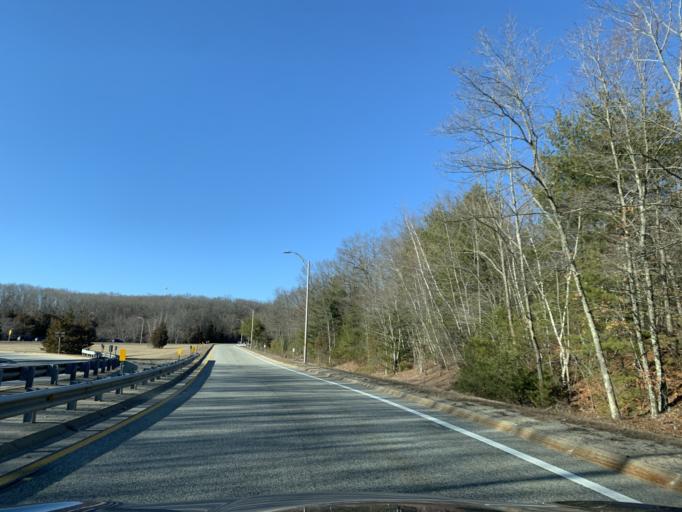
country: US
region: Rhode Island
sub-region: Providence County
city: Smithfield
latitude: 41.9086
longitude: -71.5077
